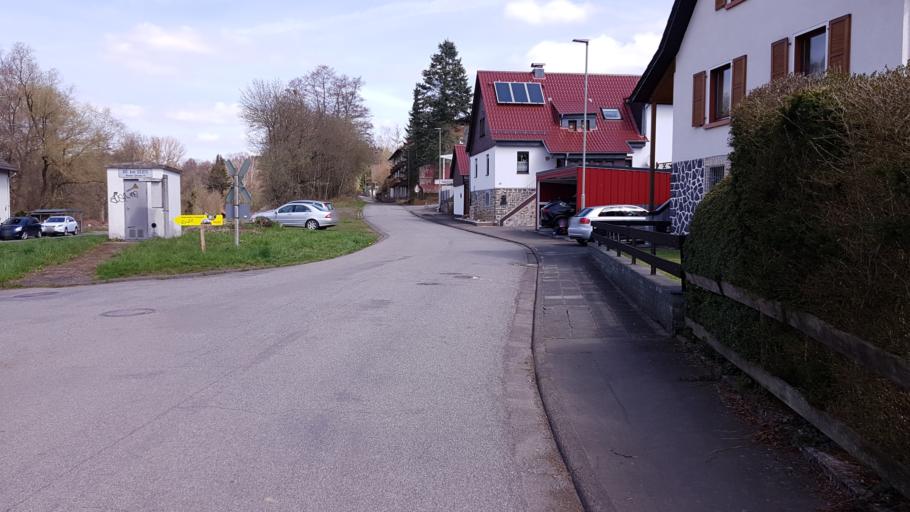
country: DE
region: Hesse
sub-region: Regierungsbezirk Giessen
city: Homberg
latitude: 50.6509
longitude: 9.0343
